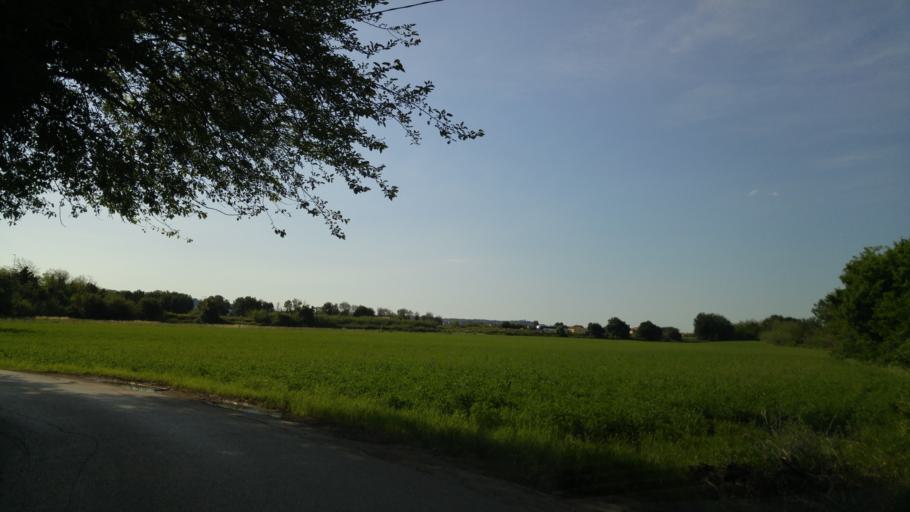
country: IT
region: The Marches
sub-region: Provincia di Pesaro e Urbino
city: Bellocchi
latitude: 43.8044
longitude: 13.0193
